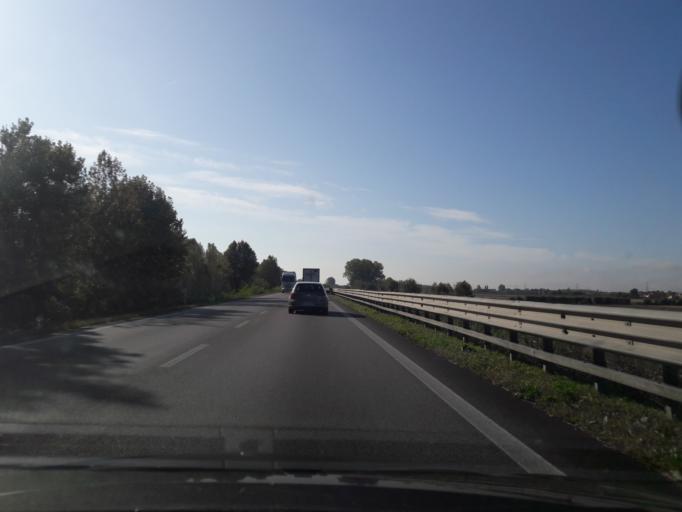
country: IT
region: Veneto
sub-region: Provincia di Venezia
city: Campagna Lupia
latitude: 45.3349
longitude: 12.1347
